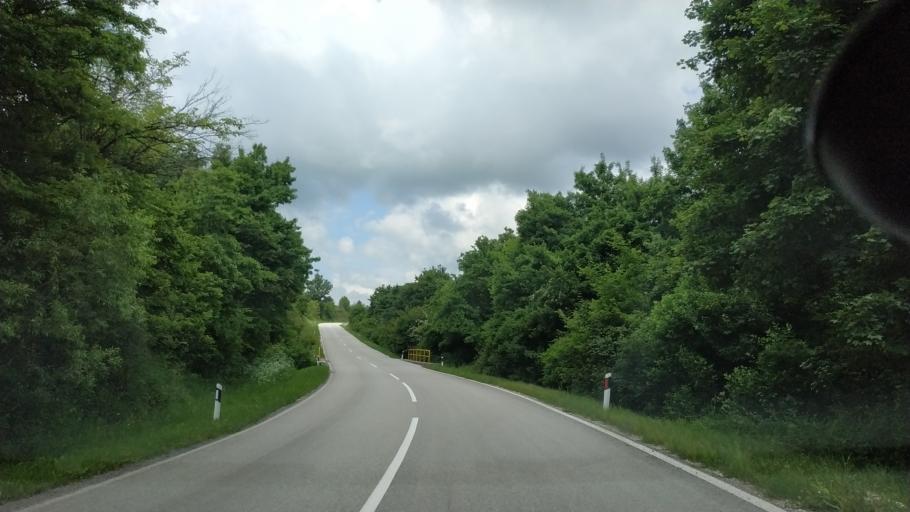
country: RS
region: Central Serbia
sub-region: Borski Okrug
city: Bor
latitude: 44.0774
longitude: 22.0243
